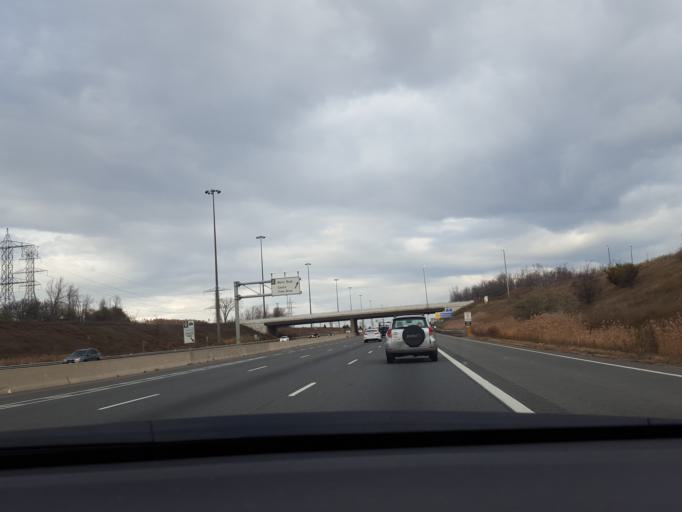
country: CA
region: Ontario
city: Mississauga
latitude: 43.5696
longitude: -79.6758
